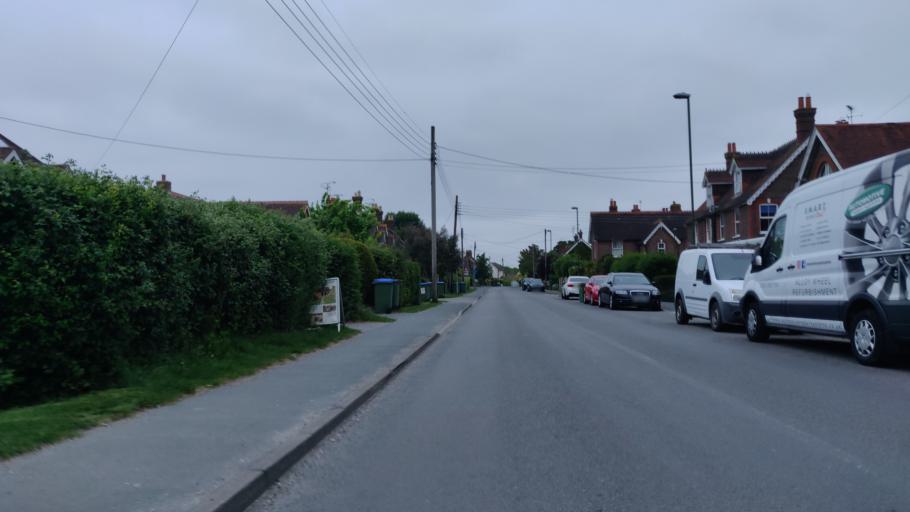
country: GB
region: England
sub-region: West Sussex
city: Partridge Green
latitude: 50.9601
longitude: -0.3036
